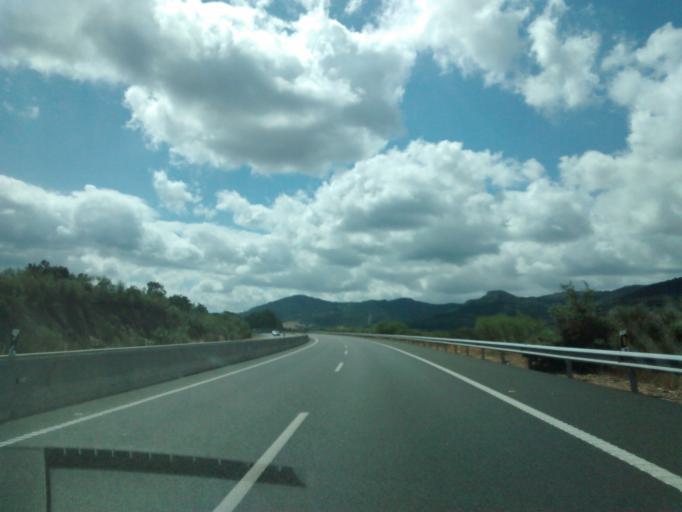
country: ES
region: Extremadura
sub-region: Provincia de Caceres
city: Romangordo
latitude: 39.7177
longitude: -5.7083
